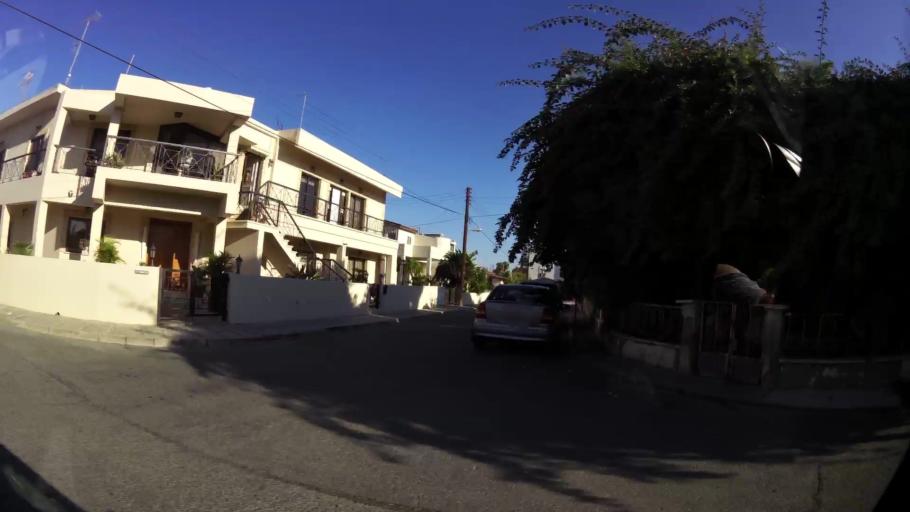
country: CY
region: Larnaka
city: Larnaca
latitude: 34.9206
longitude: 33.6181
